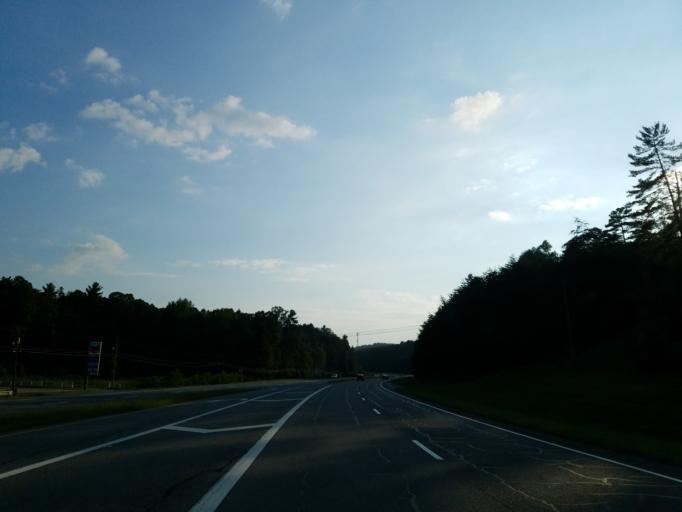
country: US
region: Georgia
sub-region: Fannin County
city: Blue Ridge
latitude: 34.8300
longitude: -84.3491
